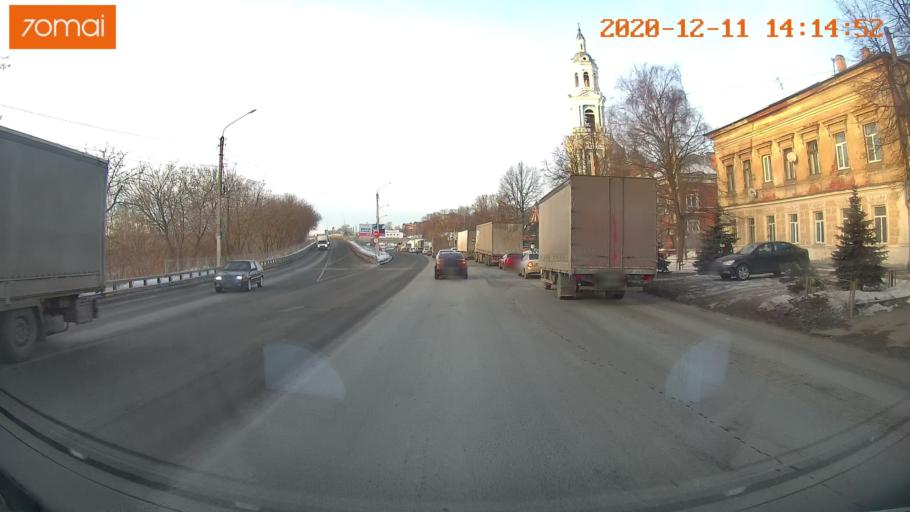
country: RU
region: Kostroma
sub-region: Kostromskoy Rayon
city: Kostroma
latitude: 57.7544
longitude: 40.9492
